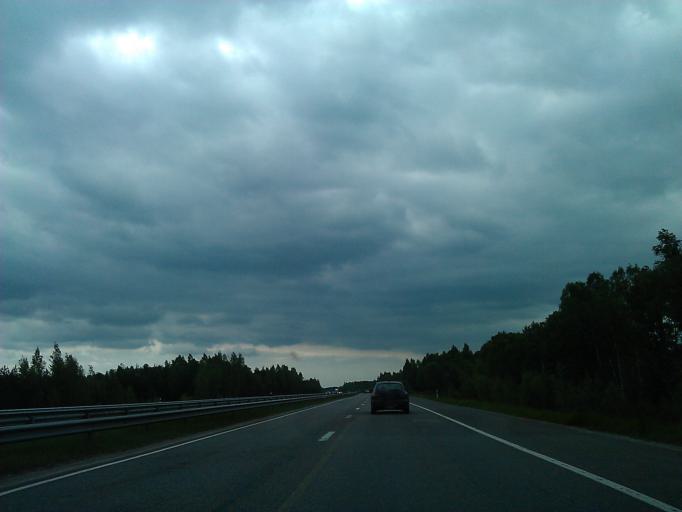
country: LV
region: Marupe
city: Marupe
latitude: 56.8717
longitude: 24.0681
